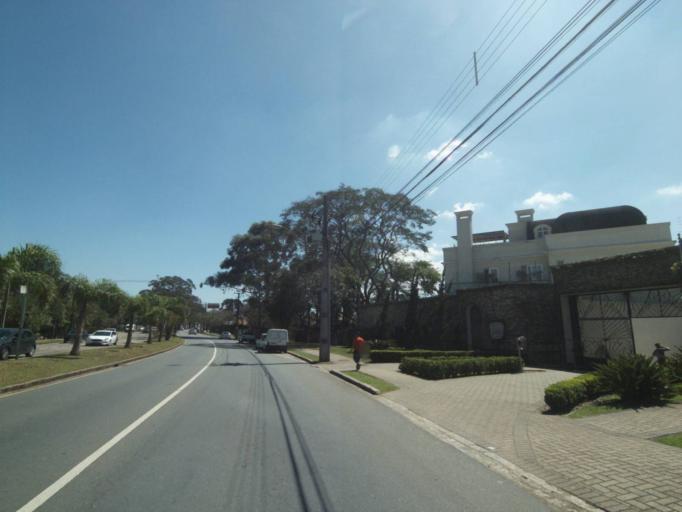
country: BR
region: Parana
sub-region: Curitiba
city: Curitiba
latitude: -25.4130
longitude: -49.2408
